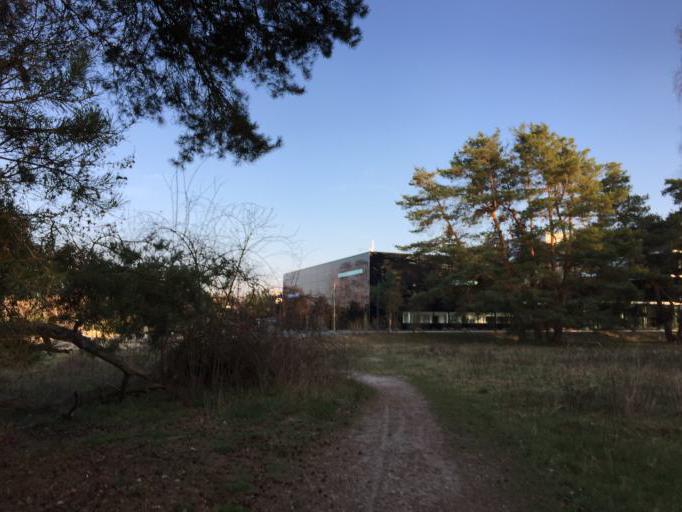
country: DE
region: Bavaria
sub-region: Regierungsbezirk Mittelfranken
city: Erlangen
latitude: 49.5835
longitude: 11.0264
